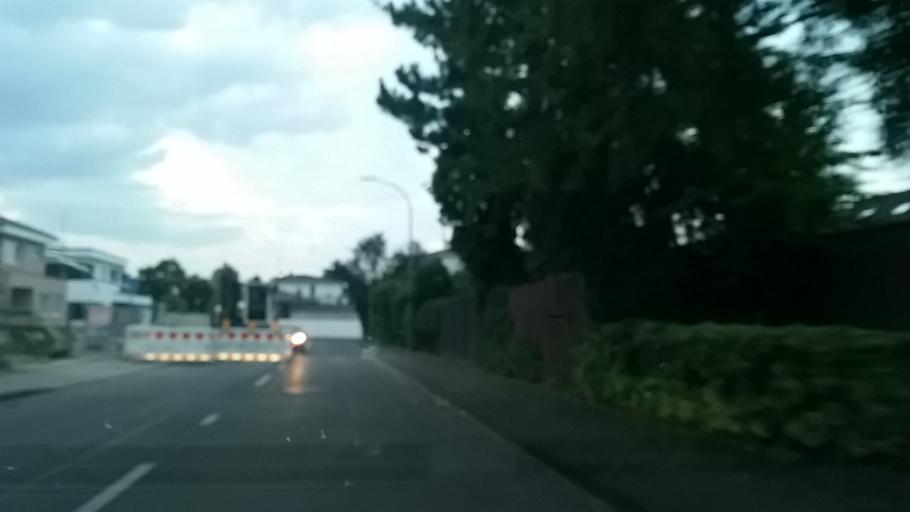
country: DE
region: North Rhine-Westphalia
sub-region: Regierungsbezirk Dusseldorf
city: Meerbusch
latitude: 51.2461
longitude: 6.6885
